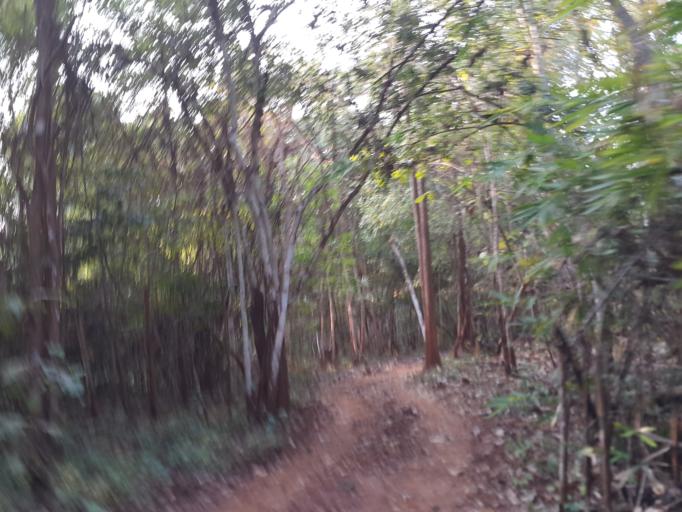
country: TH
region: Lamphun
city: Li
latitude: 17.6165
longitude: 98.8995
